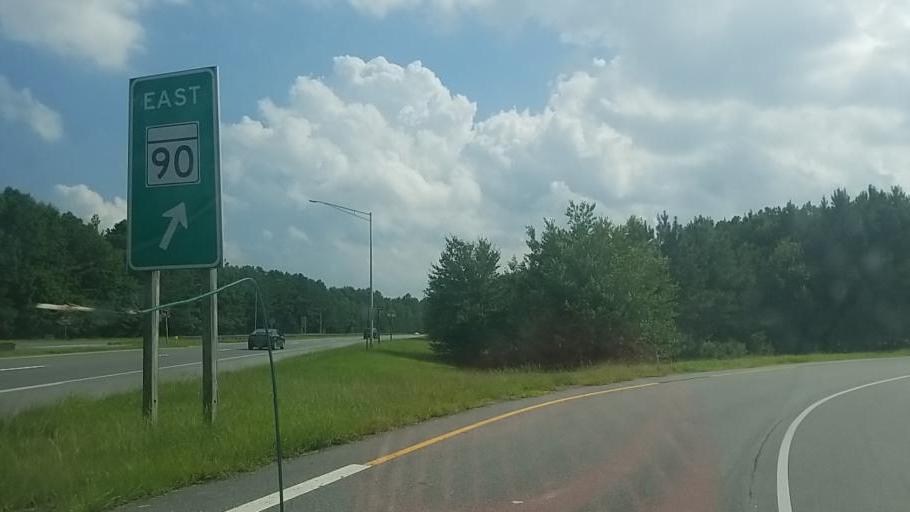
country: US
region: Maryland
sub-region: Worcester County
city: Ocean Pines
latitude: 38.3762
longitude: -75.2066
